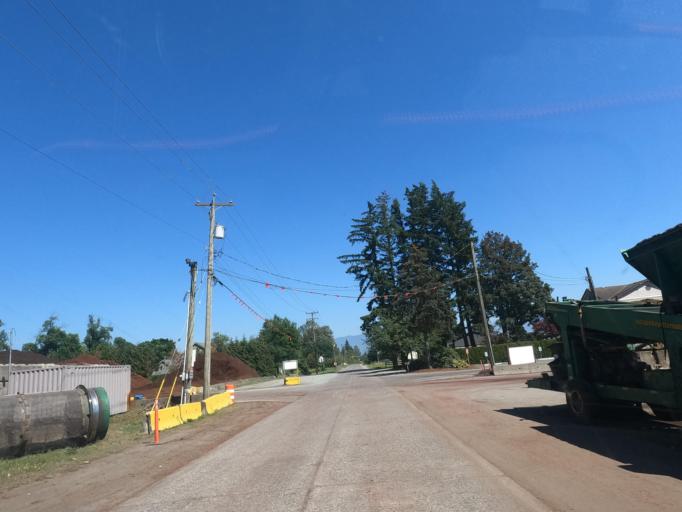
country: CA
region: British Columbia
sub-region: Fraser Valley Regional District
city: Chilliwack
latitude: 49.1256
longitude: -122.0943
